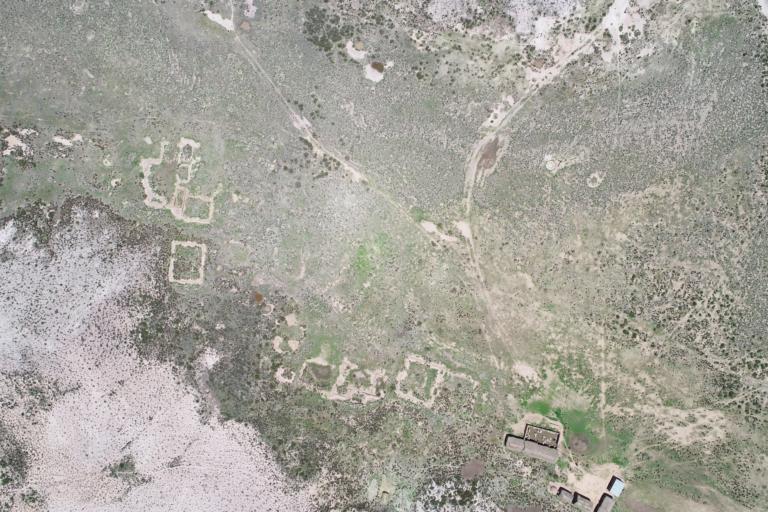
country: BO
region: La Paz
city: Patacamaya
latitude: -17.2829
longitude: -68.4972
